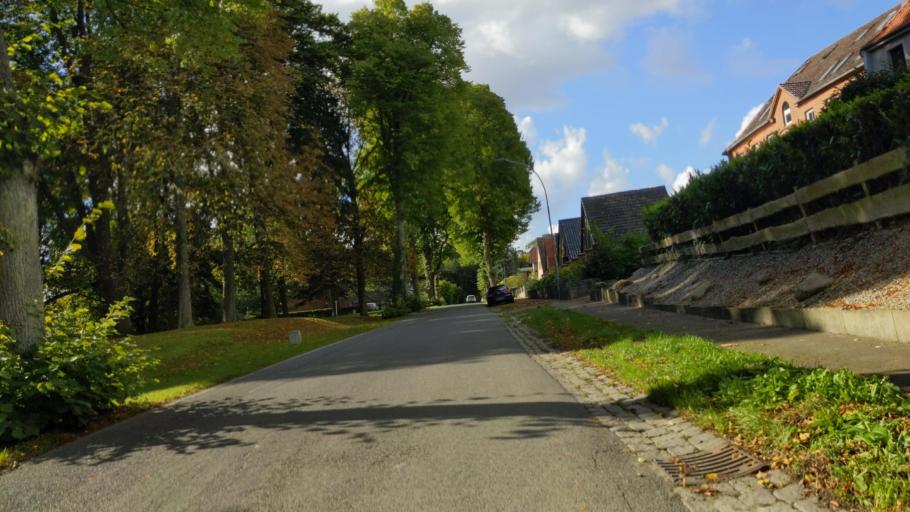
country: DE
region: Schleswig-Holstein
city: Ahrensbok
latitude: 53.9994
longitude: 10.5808
